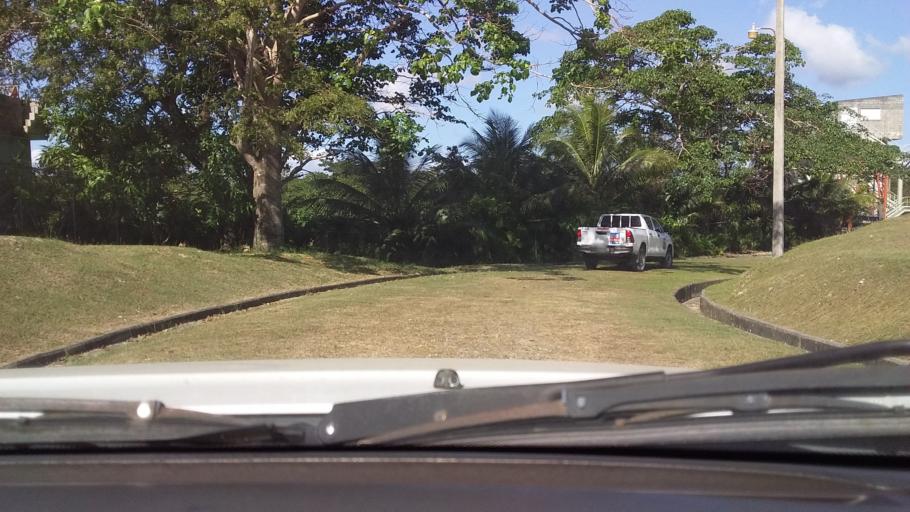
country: DO
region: Santo Domingo
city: Guerra
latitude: 18.5708
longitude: -69.7860
